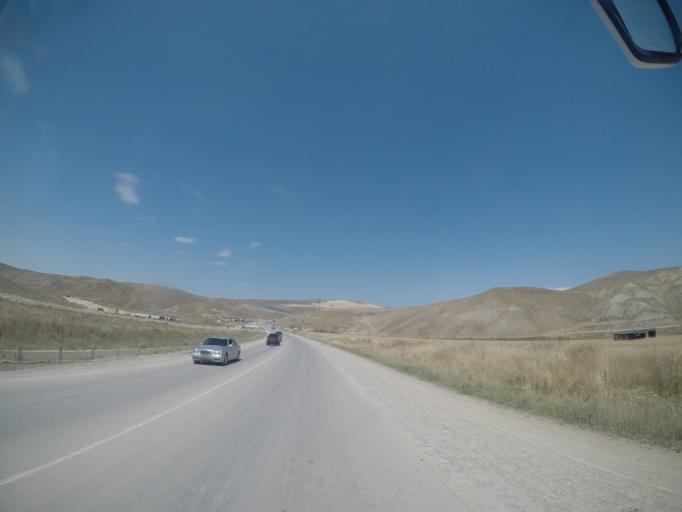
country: AZ
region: Samaxi
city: Shamakhi
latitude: 40.5554
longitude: 48.7624
